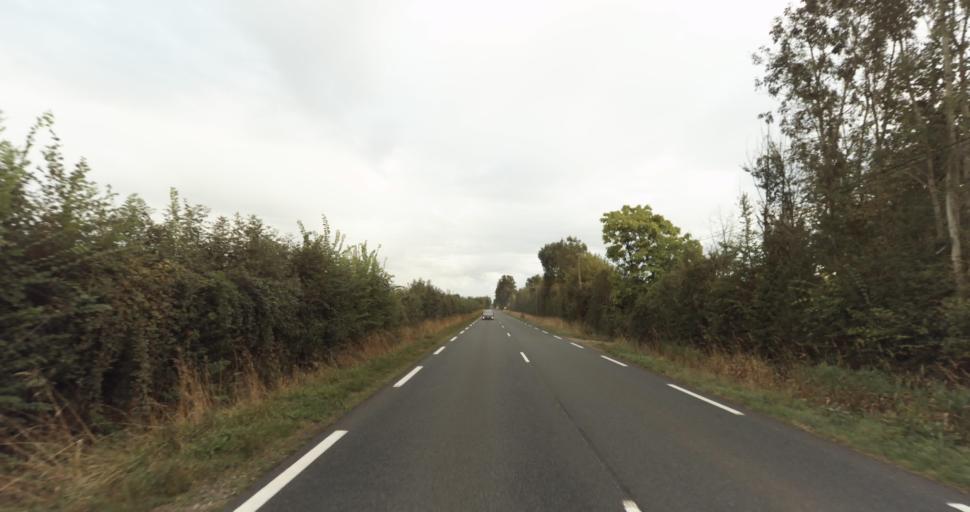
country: FR
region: Lower Normandy
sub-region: Departement de l'Orne
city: Vimoutiers
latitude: 48.8905
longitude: 0.2556
